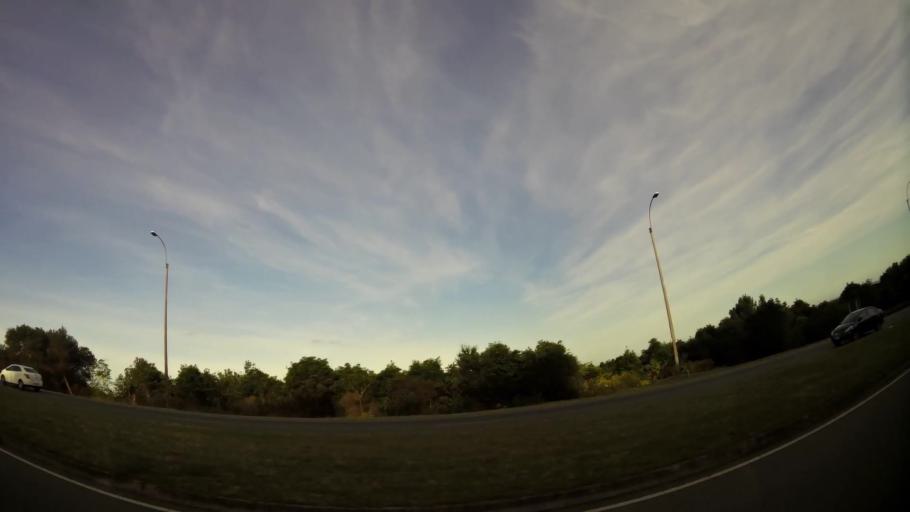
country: UY
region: Maldonado
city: Maldonado
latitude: -34.8979
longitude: -55.0375
